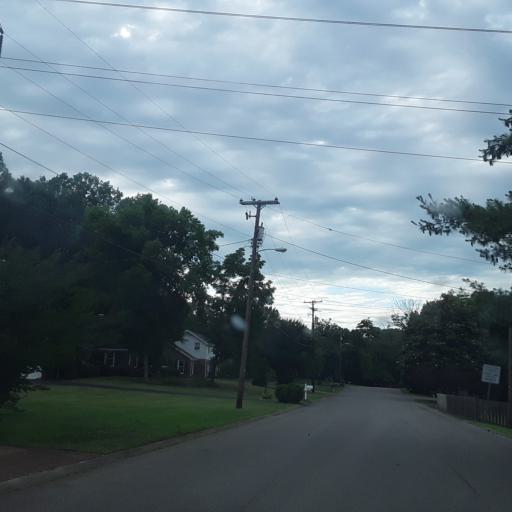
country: US
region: Tennessee
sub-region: Wilson County
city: Green Hill
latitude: 36.1653
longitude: -86.5924
